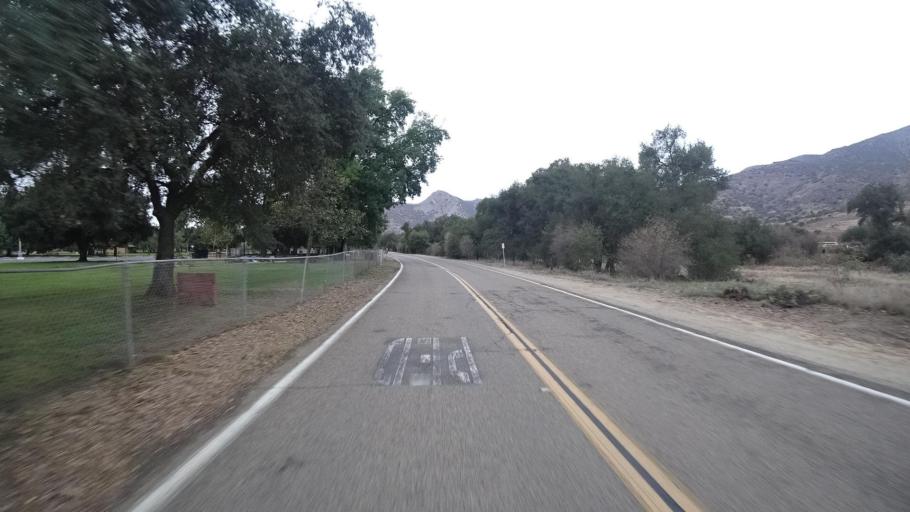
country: US
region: California
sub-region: San Diego County
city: Harbison Canyon
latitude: 32.8923
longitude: -116.8460
